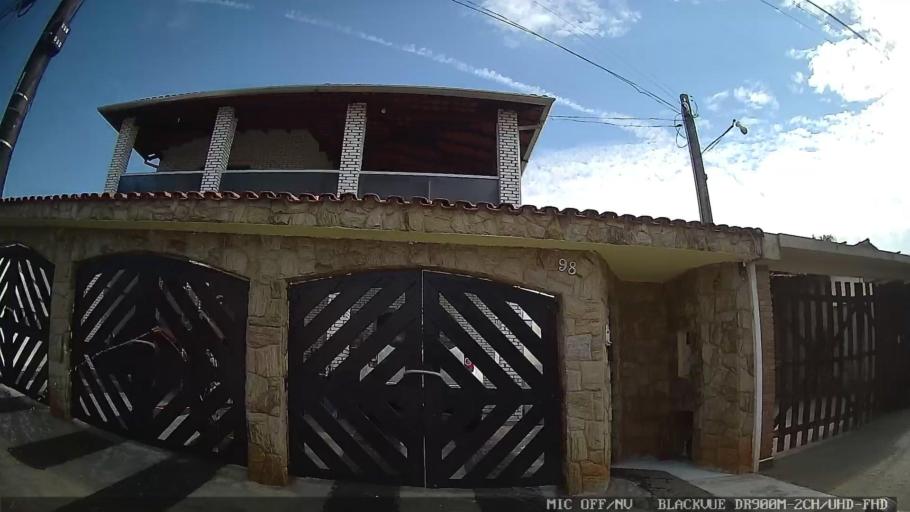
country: BR
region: Sao Paulo
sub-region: Caraguatatuba
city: Caraguatatuba
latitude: -23.6602
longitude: -45.4312
